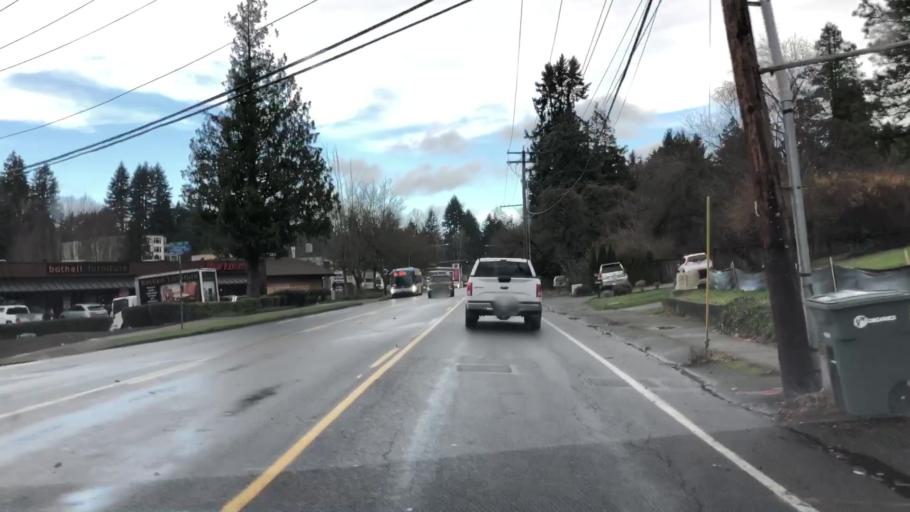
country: US
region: Washington
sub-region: King County
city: Bothell
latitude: 47.7643
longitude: -122.2083
